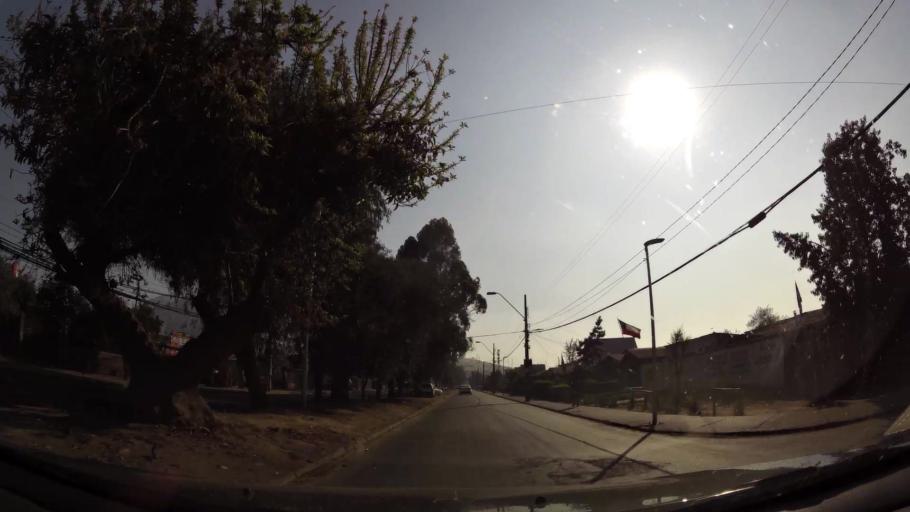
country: CL
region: Santiago Metropolitan
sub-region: Provincia de Santiago
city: Lo Prado
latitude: -33.3740
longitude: -70.6882
